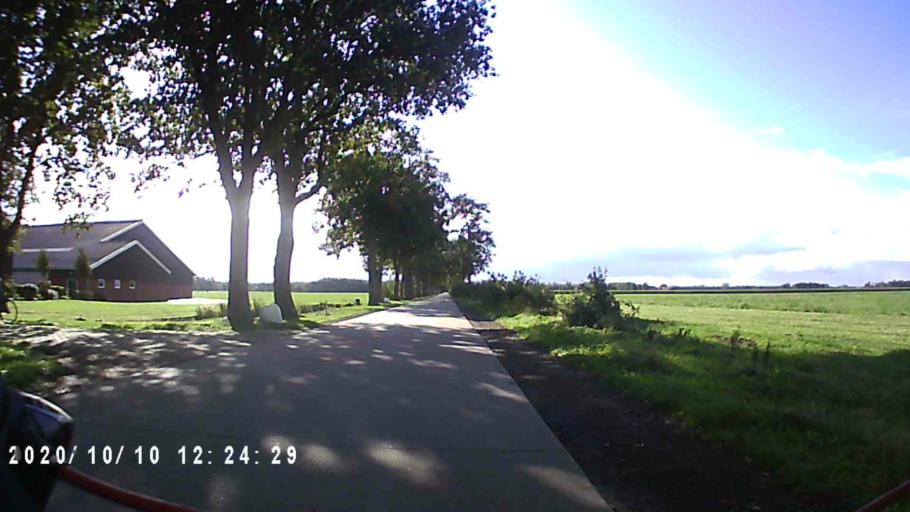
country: NL
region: Friesland
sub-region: Gemeente Heerenveen
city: Jubbega
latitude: 52.9931
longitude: 6.1802
